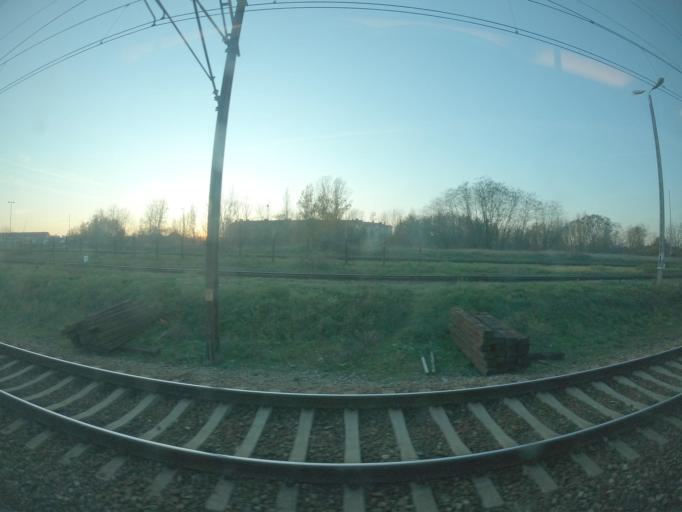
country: PL
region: Lubusz
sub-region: Powiat gorzowski
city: Kostrzyn nad Odra
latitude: 52.5971
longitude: 14.6487
